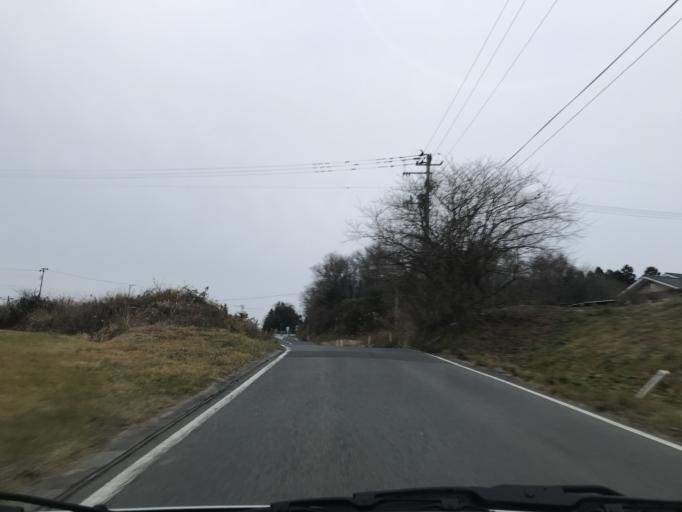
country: JP
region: Miyagi
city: Kogota
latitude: 38.6923
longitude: 141.0955
